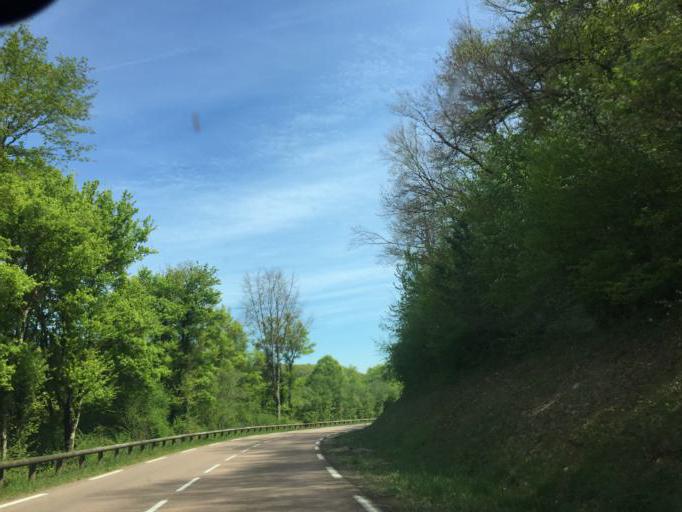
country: FR
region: Bourgogne
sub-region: Departement de l'Yonne
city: Avallon
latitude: 47.4590
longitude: 3.7165
